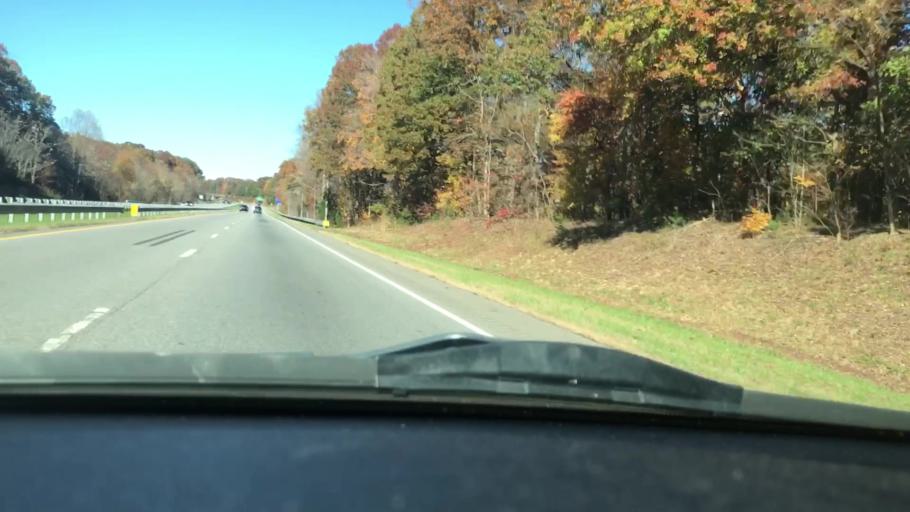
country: US
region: North Carolina
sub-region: Rockingham County
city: Madison
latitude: 36.3993
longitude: -79.9392
